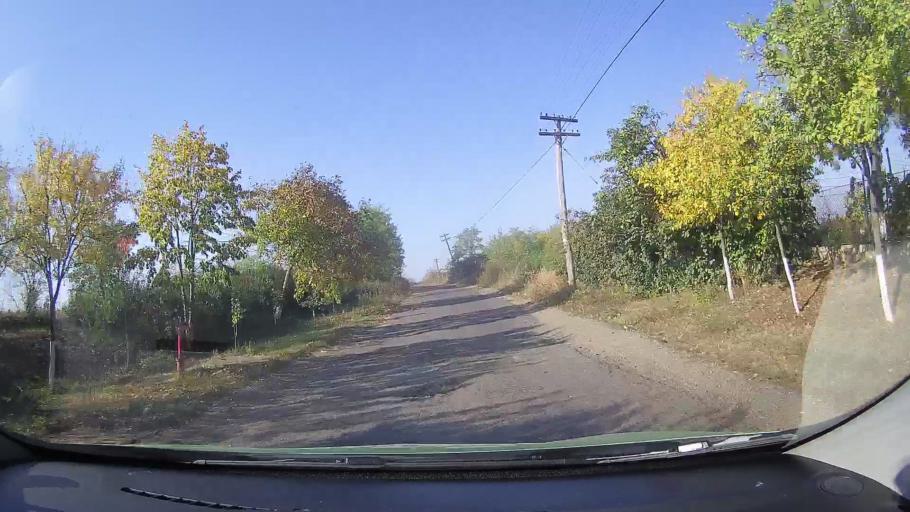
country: RO
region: Satu Mare
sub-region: Comuna Sauca
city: Sauca
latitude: 47.4706
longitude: 22.5161
